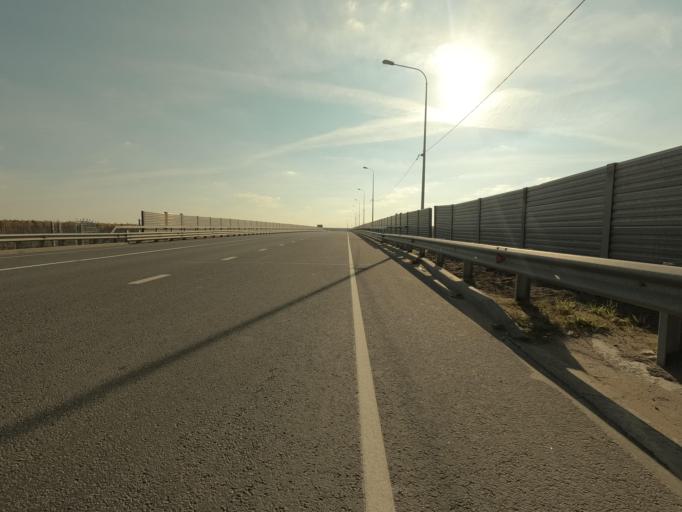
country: RU
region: Leningrad
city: Mga
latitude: 59.7559
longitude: 31.0925
